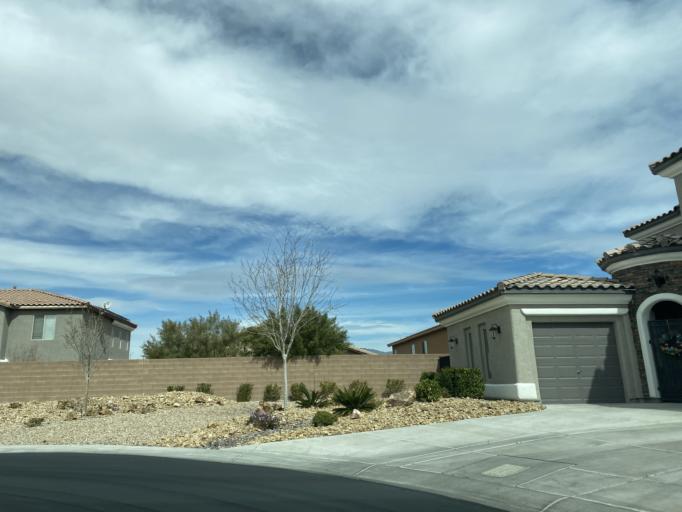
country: US
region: Nevada
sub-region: Clark County
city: Summerlin South
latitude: 36.3057
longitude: -115.3132
